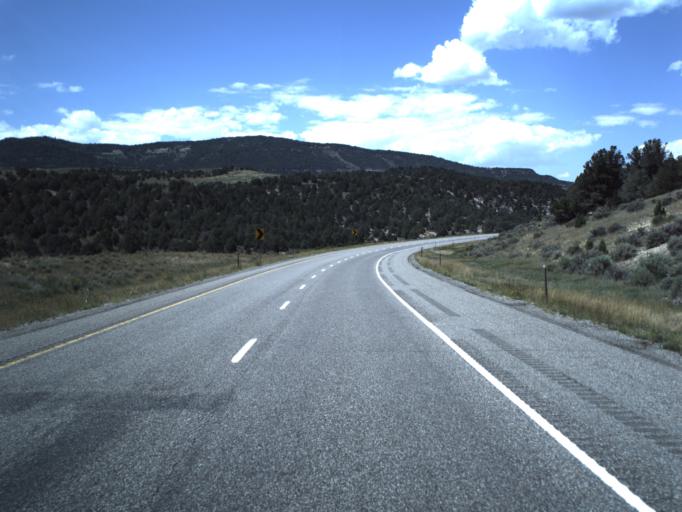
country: US
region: Utah
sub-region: Sevier County
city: Salina
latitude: 38.8519
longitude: -111.5452
